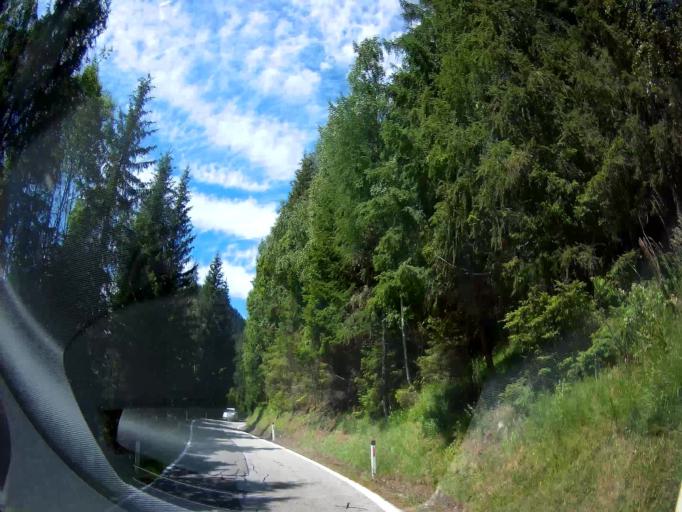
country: AT
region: Carinthia
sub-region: Politischer Bezirk Sankt Veit an der Glan
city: Glodnitz
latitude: 46.9320
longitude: 14.0539
